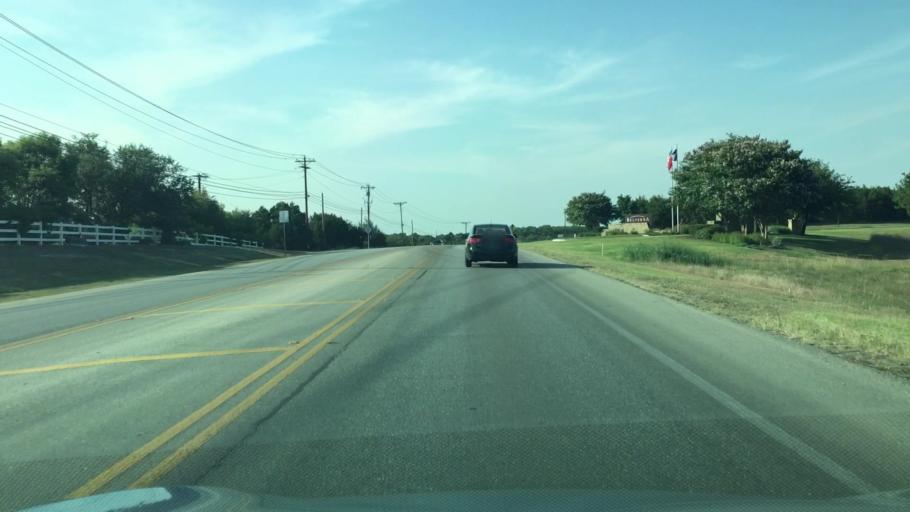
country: US
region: Texas
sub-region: Hays County
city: Dripping Springs
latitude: 30.1869
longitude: -98.0006
